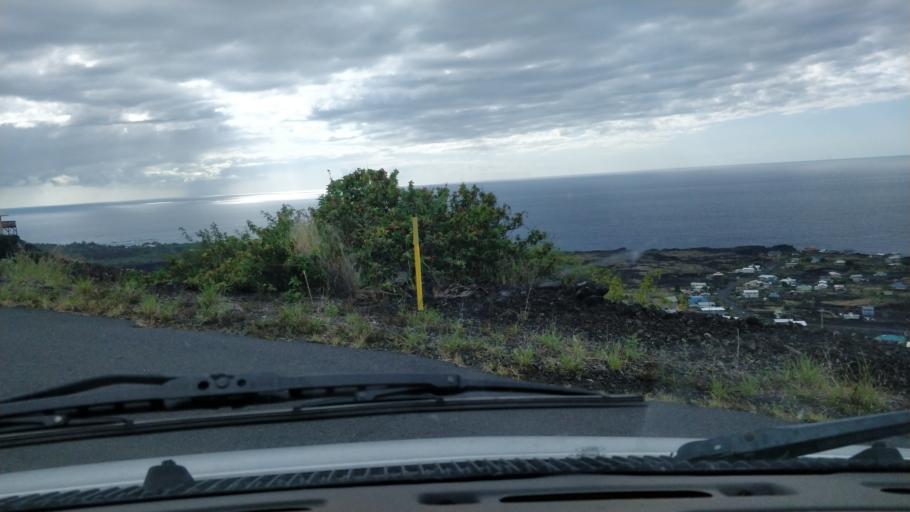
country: US
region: Hawaii
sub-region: Hawaii County
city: Hawaiian Ocean View
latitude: 19.2040
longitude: -155.8911
